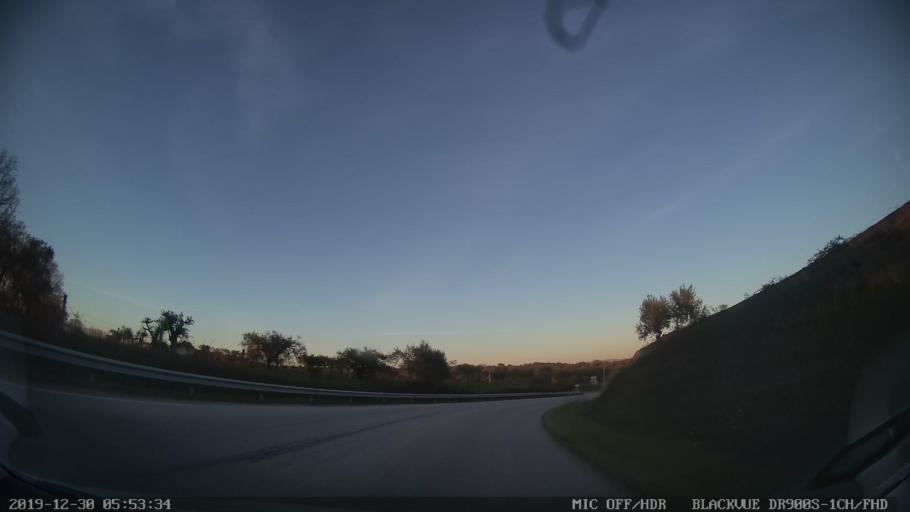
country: PT
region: Castelo Branco
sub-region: Idanha-A-Nova
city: Idanha-a-Nova
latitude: 40.0169
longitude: -7.2518
